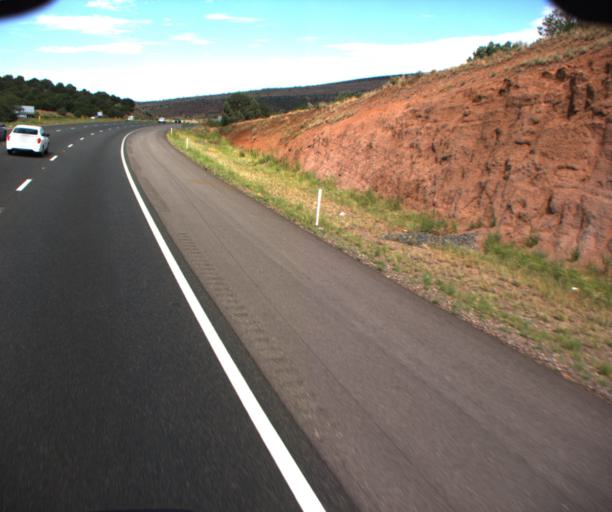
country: US
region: Arizona
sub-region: Yavapai County
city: Camp Verde
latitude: 34.5332
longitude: -111.9644
